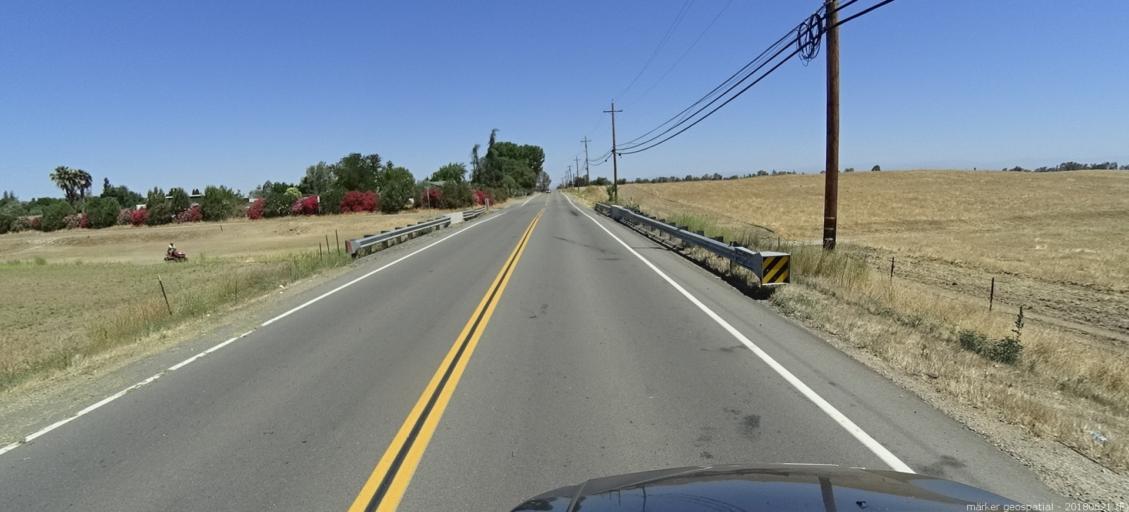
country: US
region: California
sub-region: Madera County
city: Bonadelle Ranchos-Madera Ranchos
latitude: 36.9613
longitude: -119.8939
